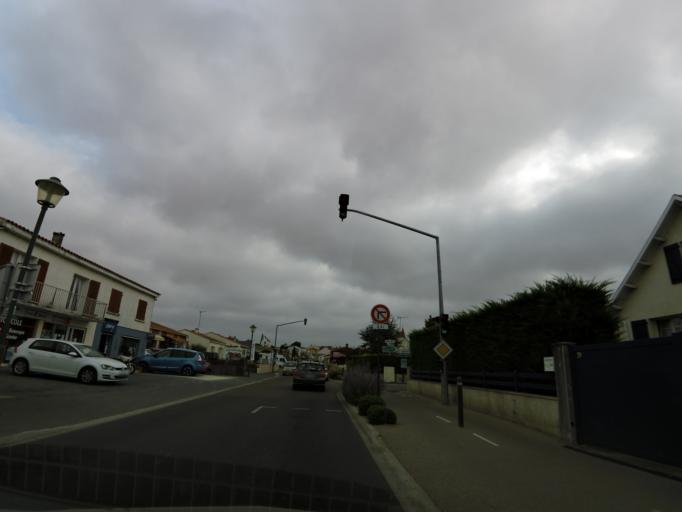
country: FR
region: Pays de la Loire
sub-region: Departement de la Vendee
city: Longeville-sur-Mer
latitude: 46.4221
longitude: -1.4926
